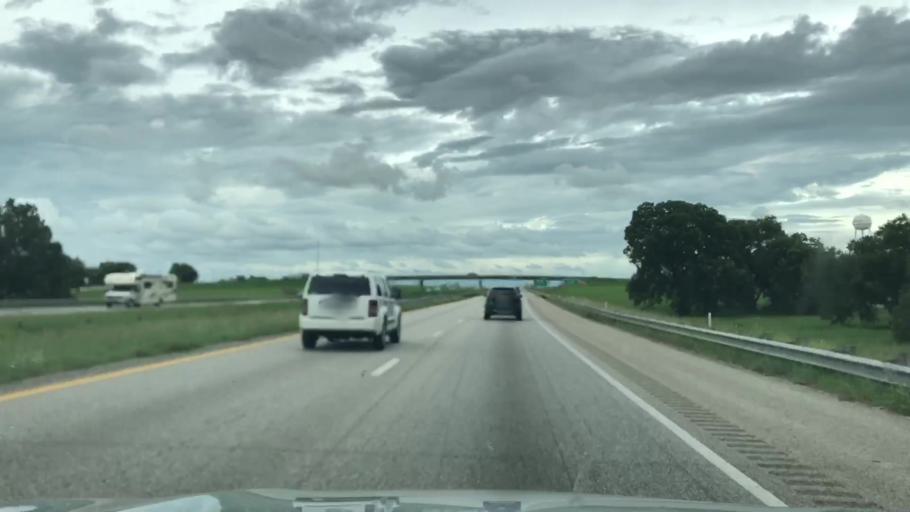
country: US
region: Texas
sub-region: Guadalupe County
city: McQueeney
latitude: 29.5698
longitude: -98.0179
